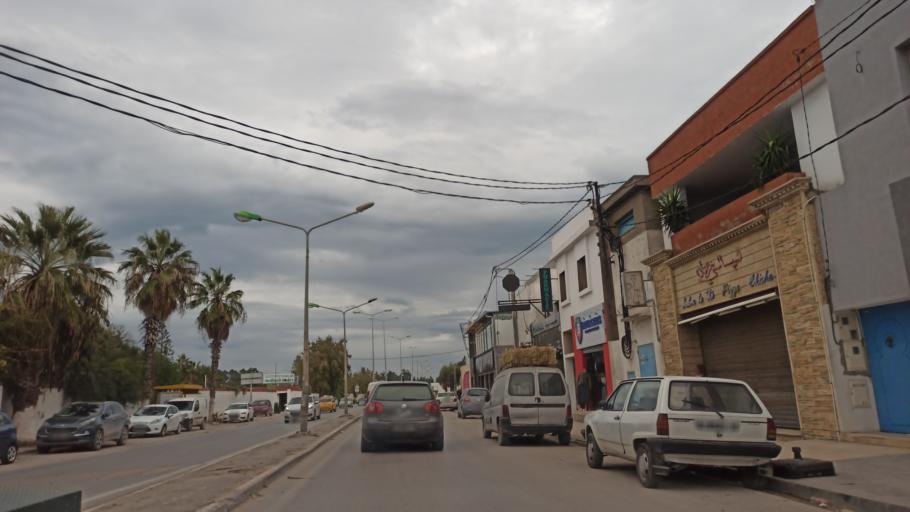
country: TN
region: Ariana
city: Ariana
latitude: 36.8733
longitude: 10.2367
